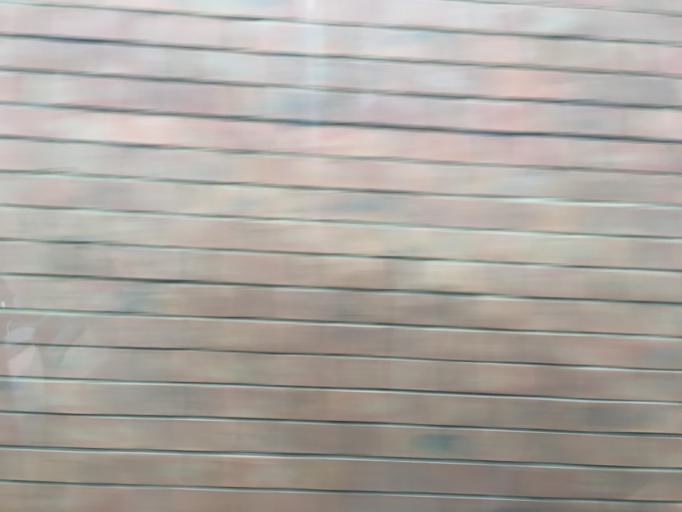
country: GT
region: Guatemala
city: Villa Canales
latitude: 14.4491
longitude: -90.5658
